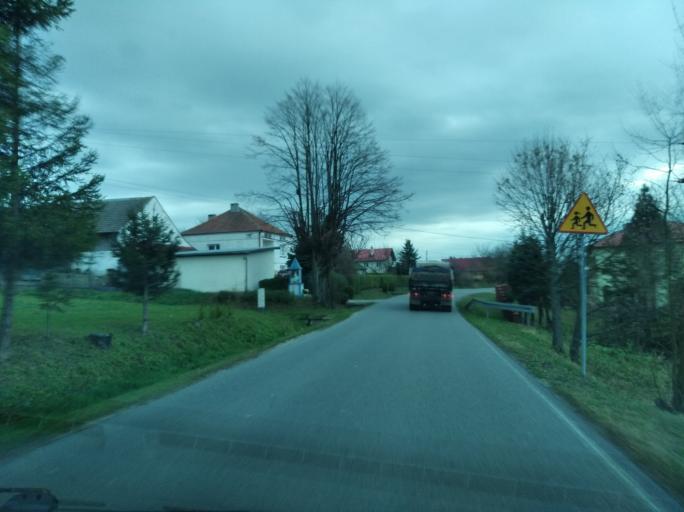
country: PL
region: Subcarpathian Voivodeship
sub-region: Powiat strzyzowski
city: Wisniowa
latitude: 49.9383
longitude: 21.6948
